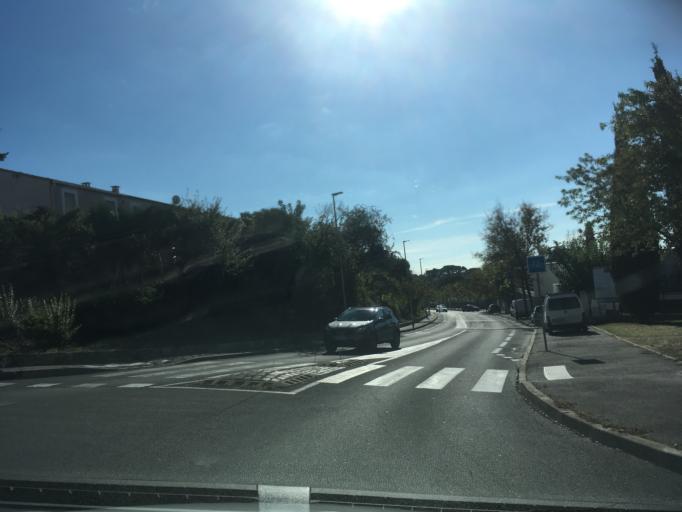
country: FR
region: Languedoc-Roussillon
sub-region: Departement de l'Herault
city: Juvignac
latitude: 43.6070
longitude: 3.8320
